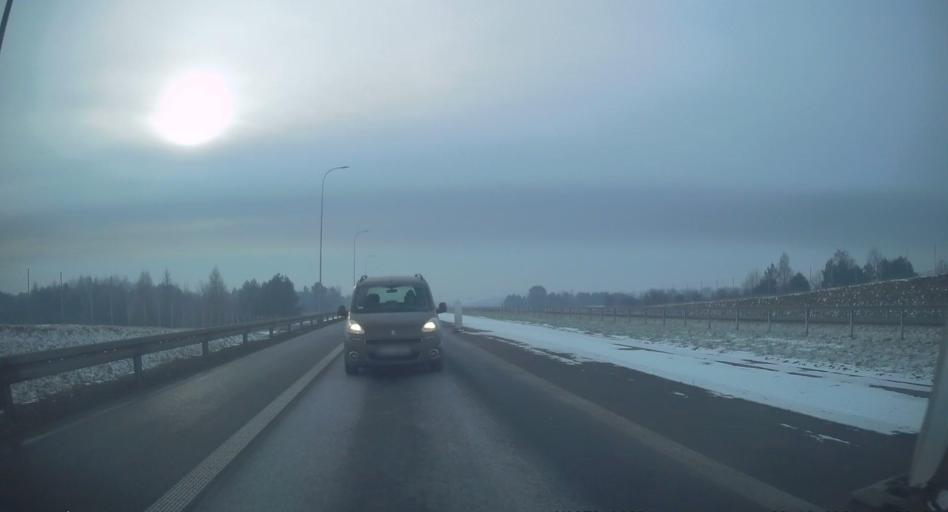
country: PL
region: Lesser Poland Voivodeship
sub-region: Powiat miechowski
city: Miechow
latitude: 50.3090
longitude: 20.0330
